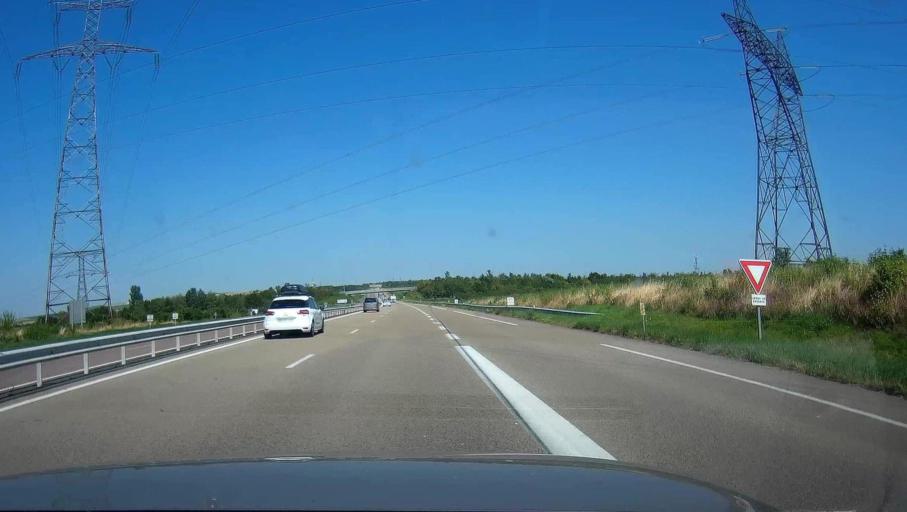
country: FR
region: Champagne-Ardenne
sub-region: Departement de l'Aube
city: Creney-pres-Troyes
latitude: 48.3344
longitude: 4.1672
